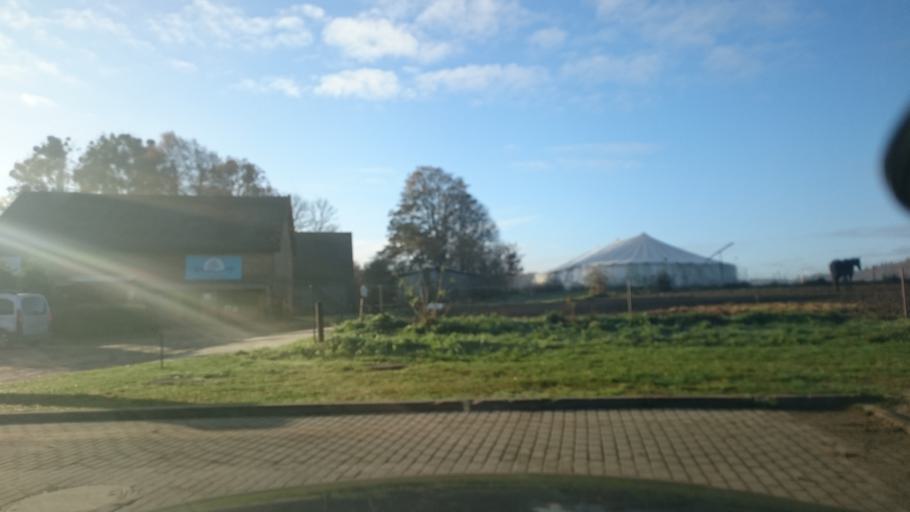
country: PL
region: Pomeranian Voivodeship
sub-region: Gdynia
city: Wielki Kack
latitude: 54.4610
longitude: 18.4932
